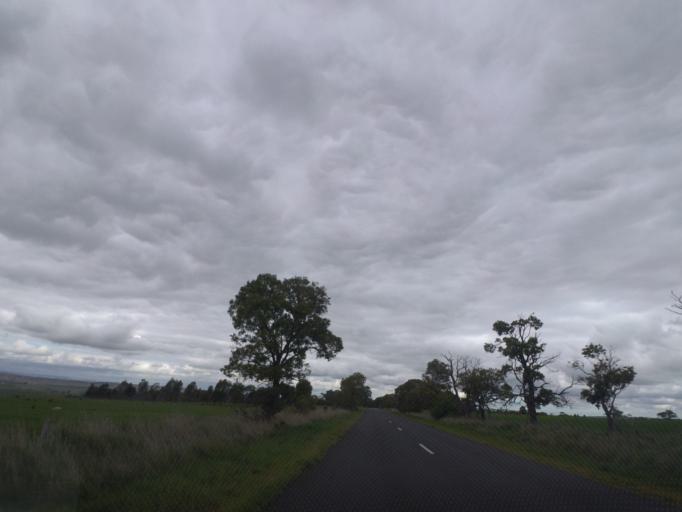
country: AU
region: Victoria
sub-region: Hume
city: Sunbury
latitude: -37.3916
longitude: 144.8330
